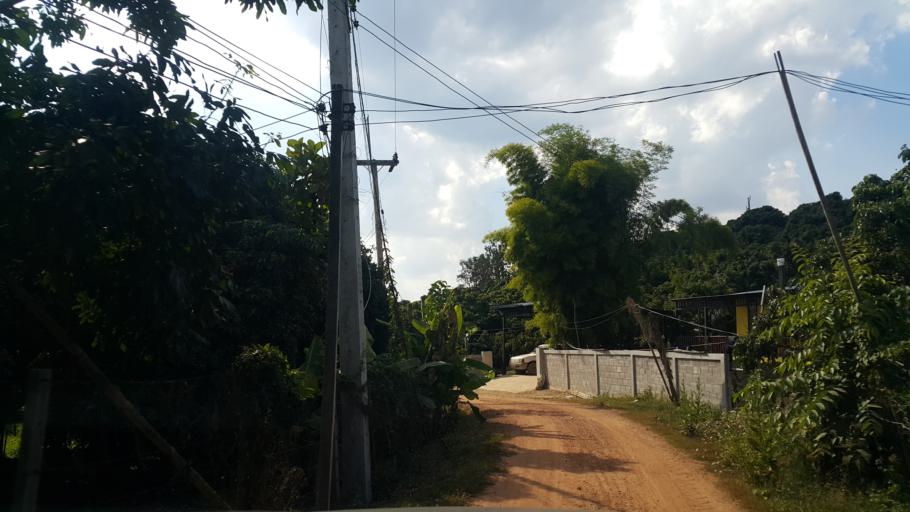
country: TH
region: Lamphun
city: Ban Thi
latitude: 18.5964
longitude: 99.1579
